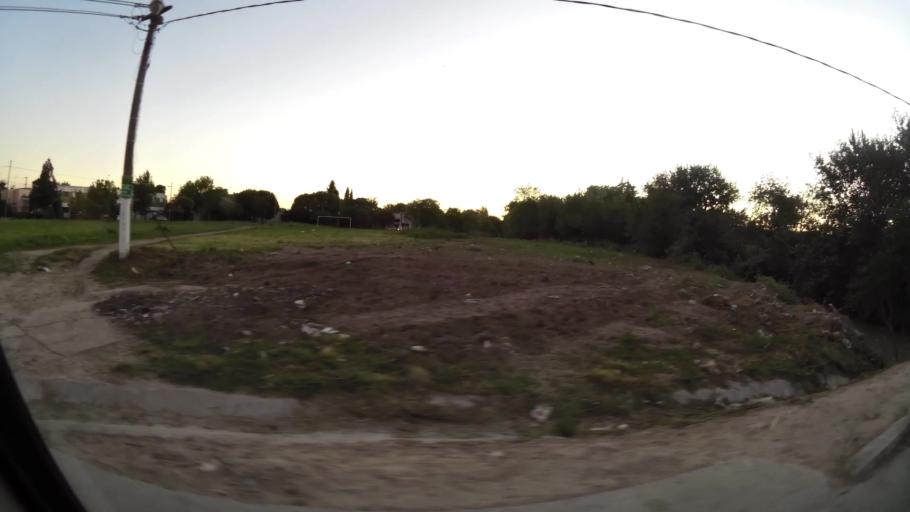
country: AR
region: Buenos Aires
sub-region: Partido de Quilmes
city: Quilmes
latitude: -34.8023
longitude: -58.1906
